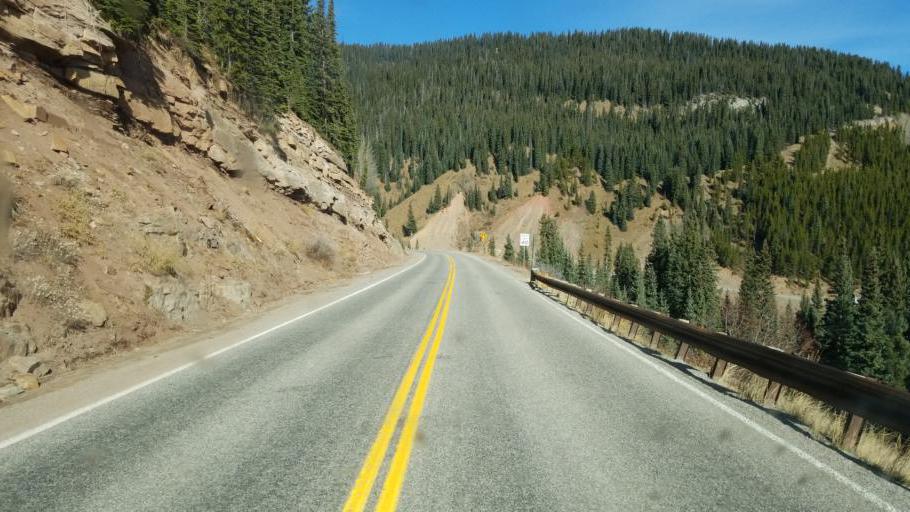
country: US
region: Colorado
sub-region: San Juan County
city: Silverton
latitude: 37.7042
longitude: -107.7685
